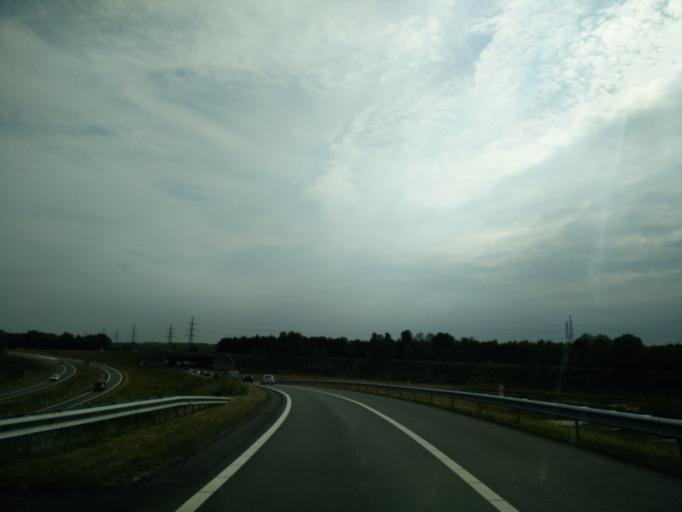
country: NL
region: Drenthe
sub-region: Gemeente Assen
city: Assen
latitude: 52.9700
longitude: 6.5487
